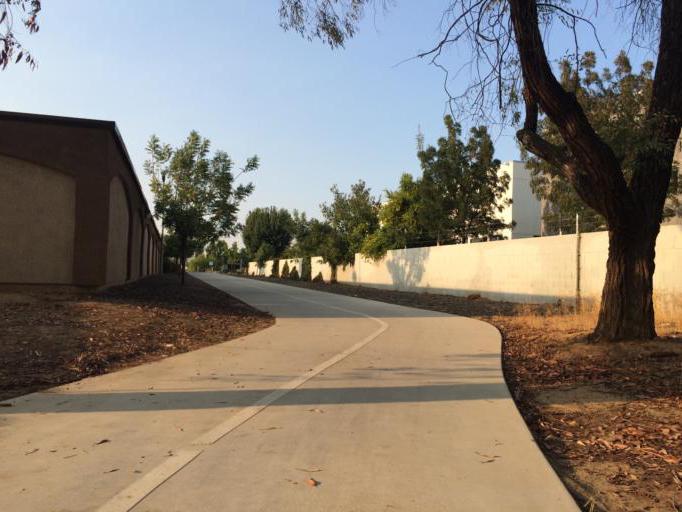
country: US
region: California
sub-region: Fresno County
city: Fresno
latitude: 36.8459
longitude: -119.8107
